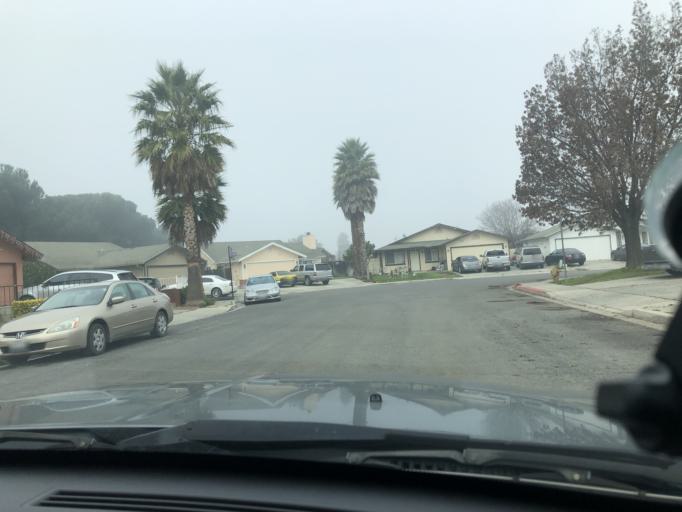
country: US
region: California
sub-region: Monterey County
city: King City
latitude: 36.2052
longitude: -121.1443
